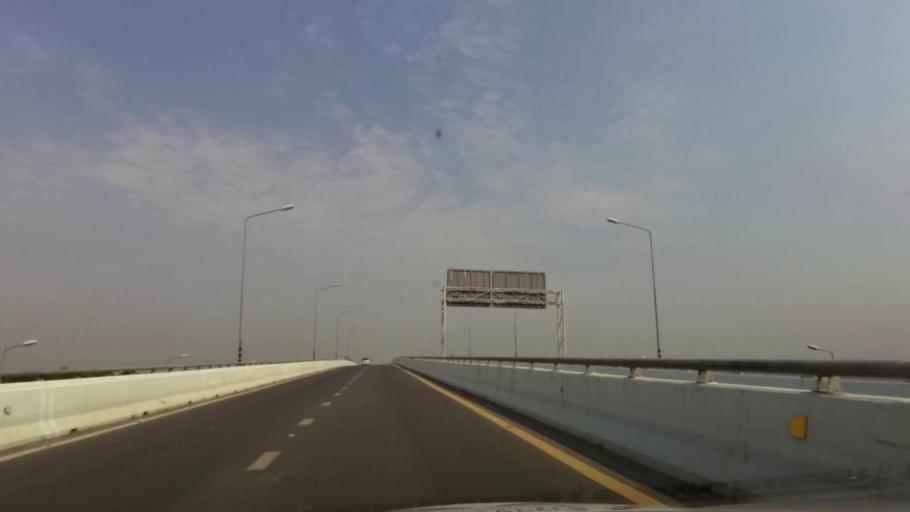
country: TH
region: Phra Nakhon Si Ayutthaya
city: Phra Nakhon Si Ayutthaya
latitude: 14.3307
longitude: 100.5819
